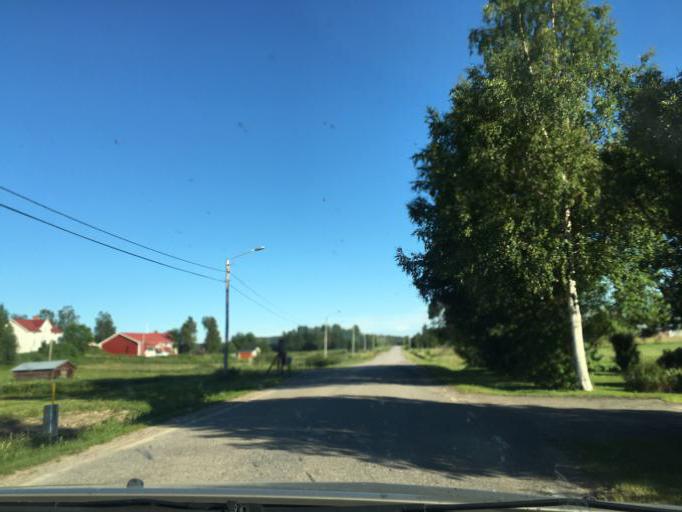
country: SE
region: Norrbotten
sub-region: Kalix Kommun
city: Rolfs
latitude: 65.8978
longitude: 22.9379
